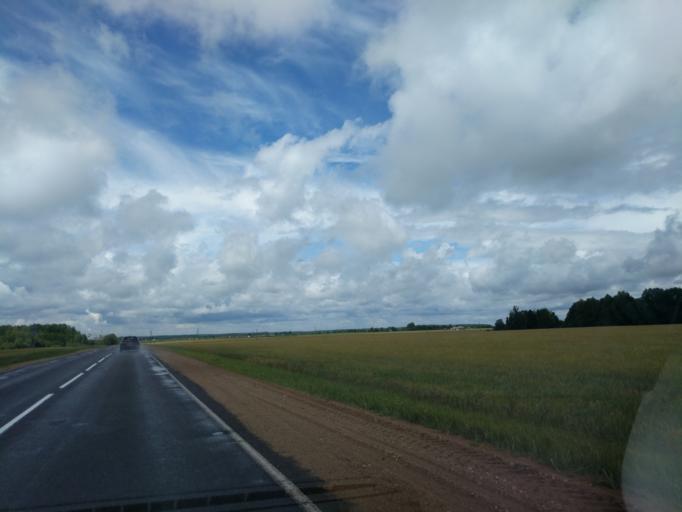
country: BY
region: Minsk
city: Il'ya
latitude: 54.3824
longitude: 27.3685
